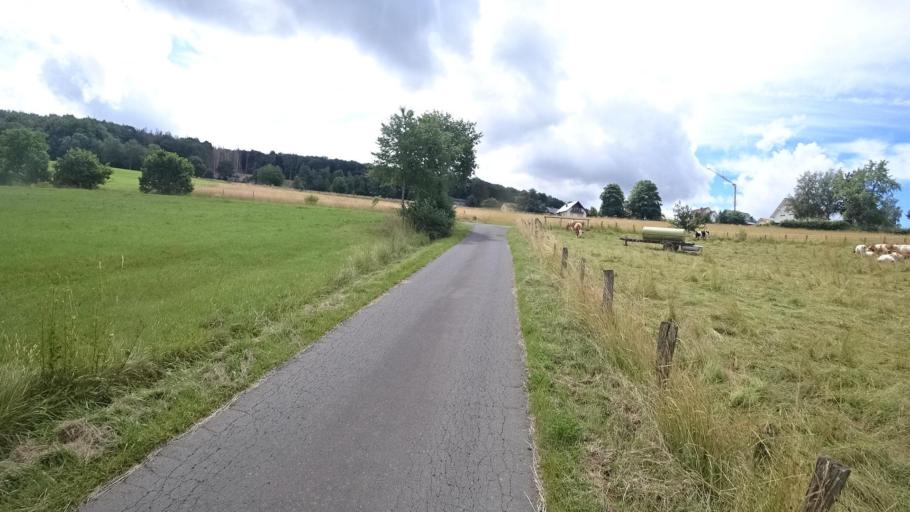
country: DE
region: Rheinland-Pfalz
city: Kircheib
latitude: 50.7211
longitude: 7.4566
